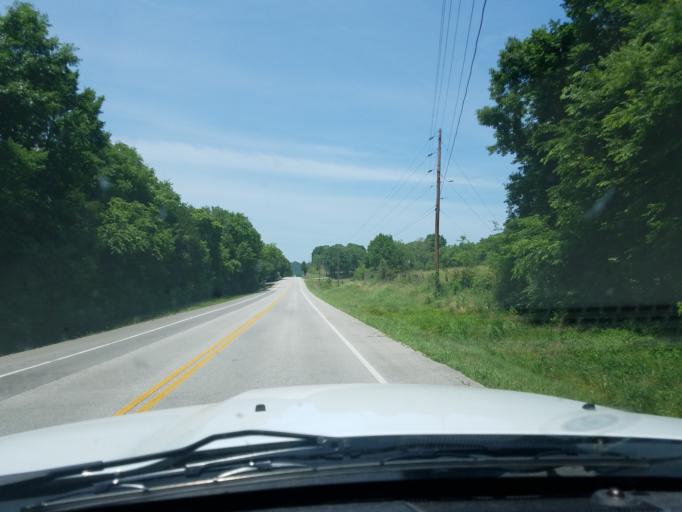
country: US
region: Tennessee
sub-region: Trousdale County
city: Hartsville
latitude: 36.4397
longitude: -86.2667
